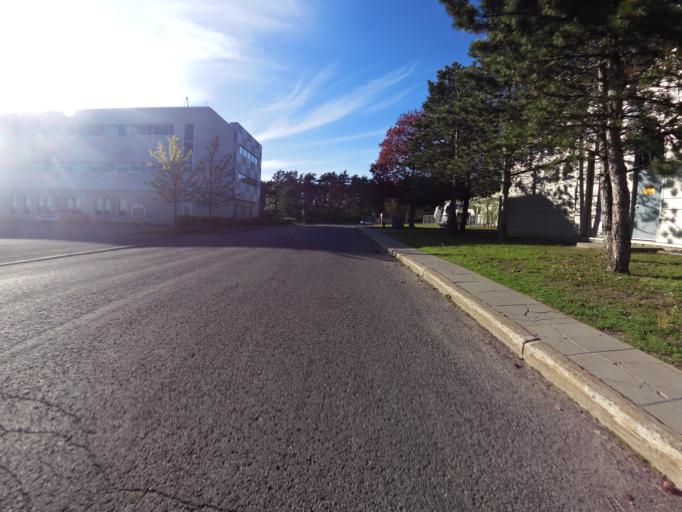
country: CA
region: Ontario
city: Ottawa
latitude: 45.3354
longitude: -75.6883
